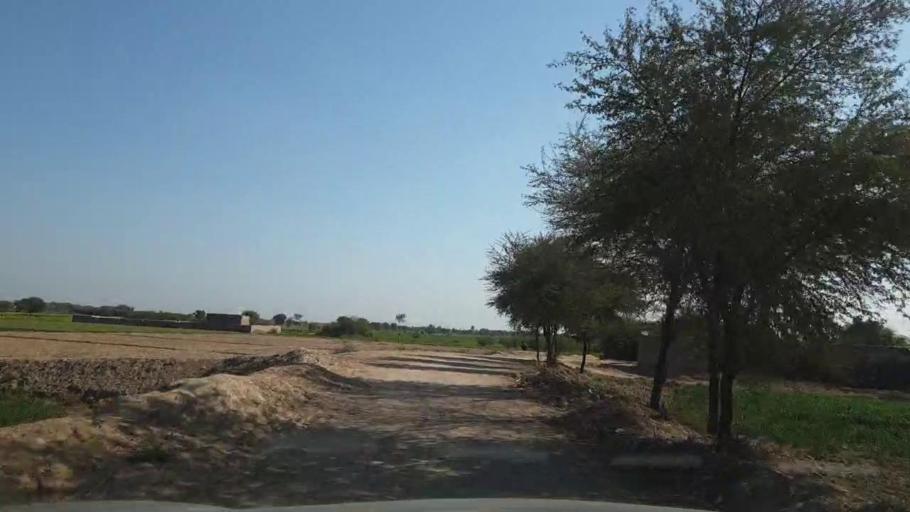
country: PK
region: Sindh
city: Tando Adam
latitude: 25.6620
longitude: 68.6934
